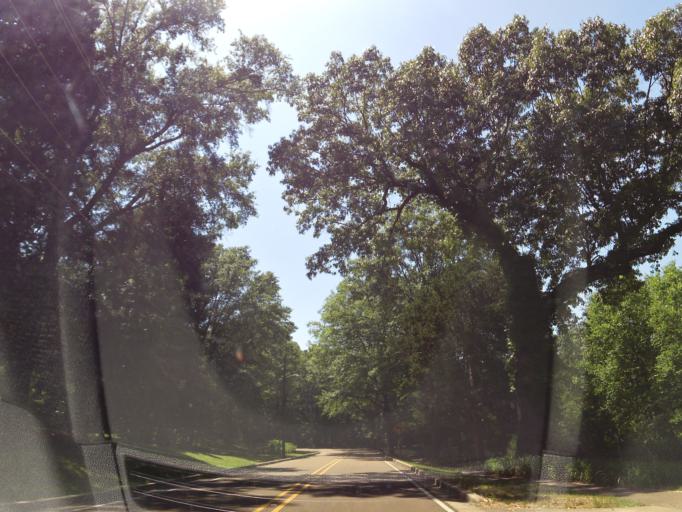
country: US
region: Mississippi
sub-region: Lafayette County
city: University
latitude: 34.3585
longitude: -89.5229
